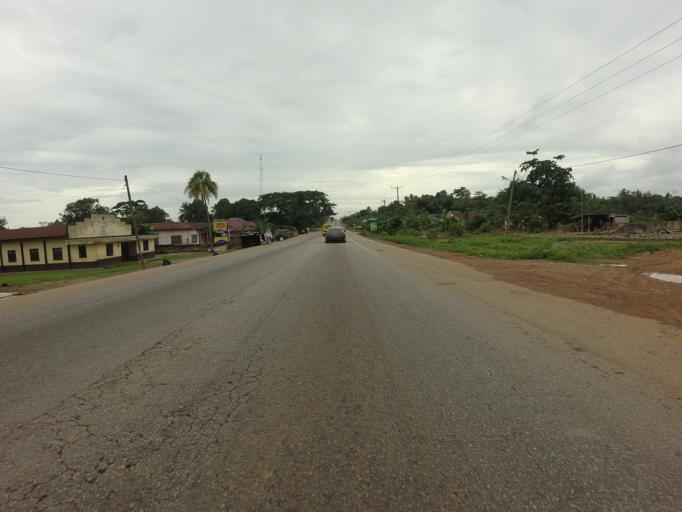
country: GH
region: Eastern
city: Nkawkaw
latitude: 6.4751
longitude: -0.6531
